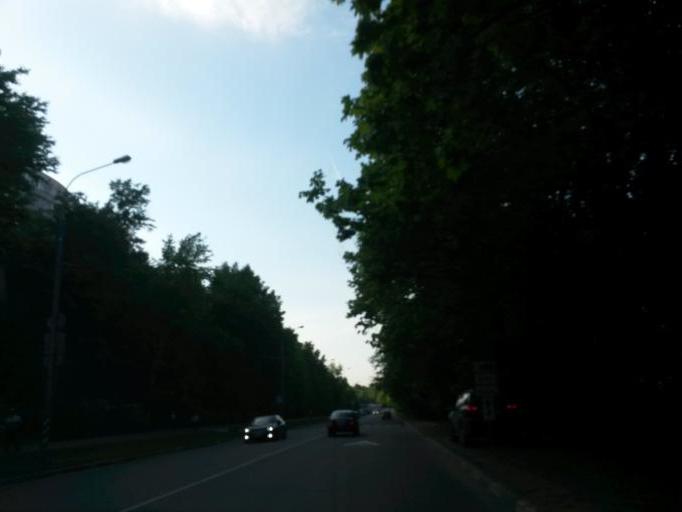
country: RU
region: Moskovskaya
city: Biryulevo Zapadnoye
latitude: 55.5886
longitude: 37.6558
